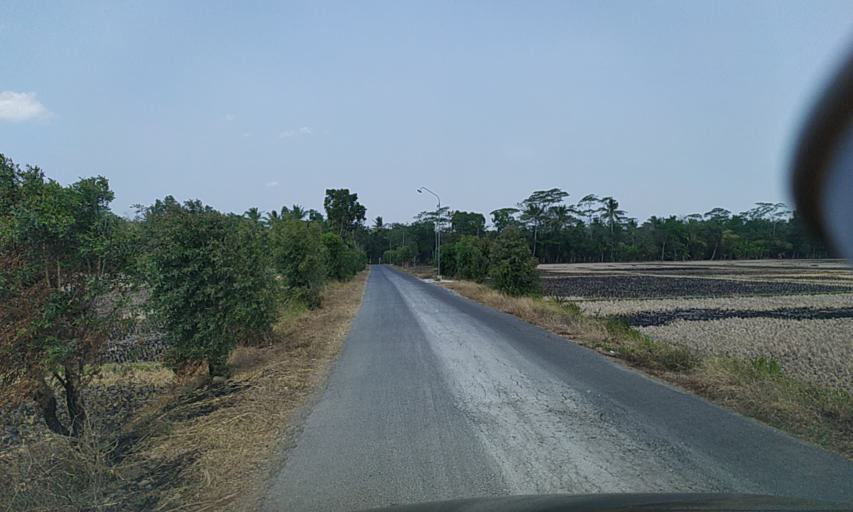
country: ID
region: Central Java
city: Ciklapa
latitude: -7.5040
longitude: 108.7987
